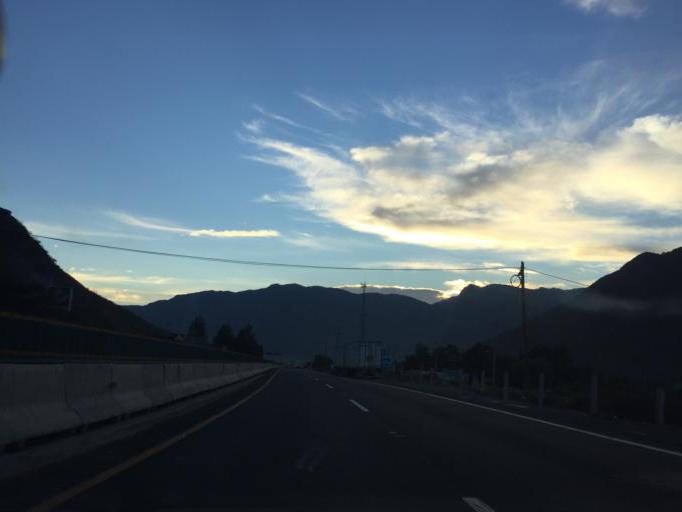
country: MX
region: Veracruz
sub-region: Nogales
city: Agricola Lazaro Cardenas
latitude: 18.8178
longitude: -97.2248
